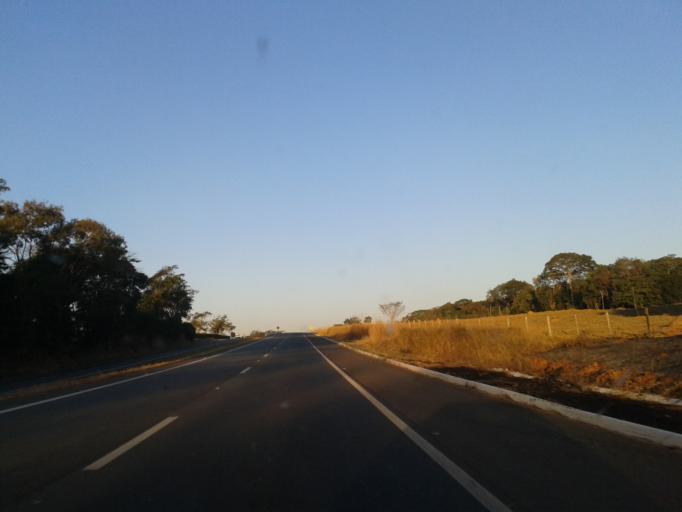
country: BR
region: Goias
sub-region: Itaberai
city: Itaberai
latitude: -16.0148
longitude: -49.8945
